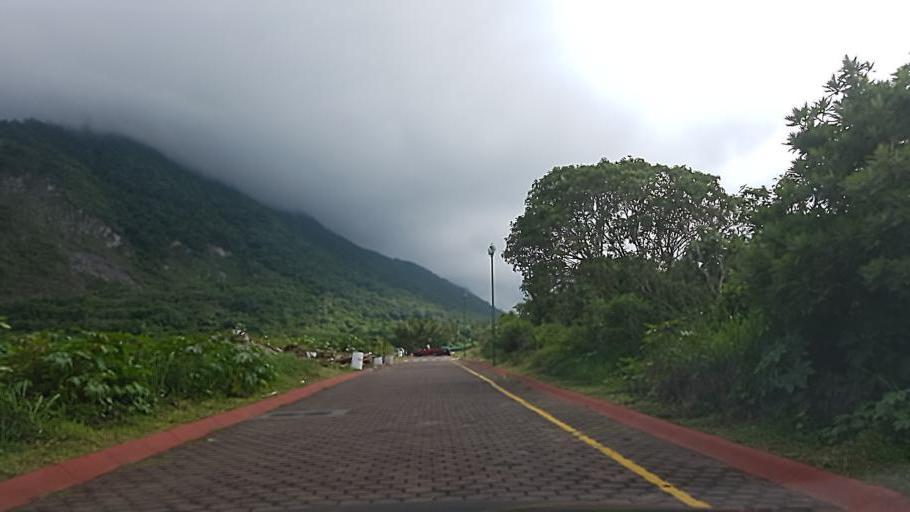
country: MX
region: Nayarit
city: Tepic
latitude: 21.5180
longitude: -104.9305
